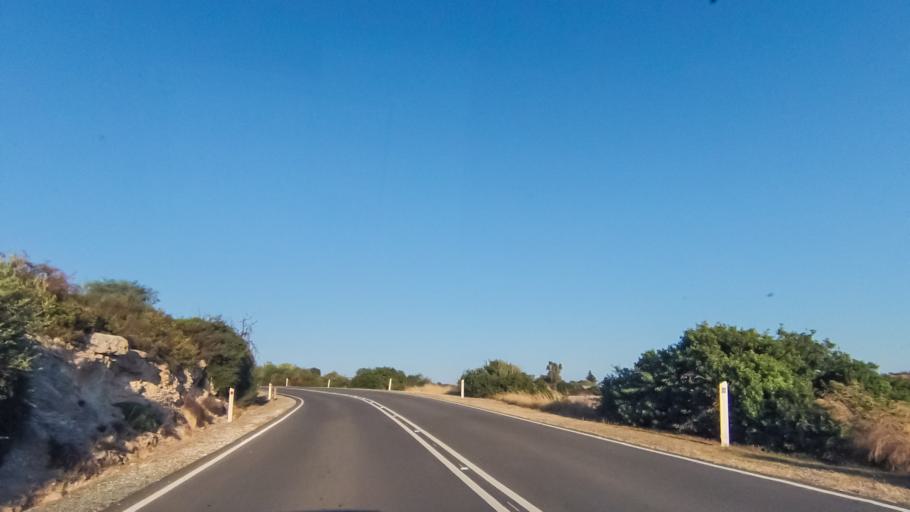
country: CY
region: Limassol
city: Sotira
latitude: 34.6752
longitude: 32.8076
